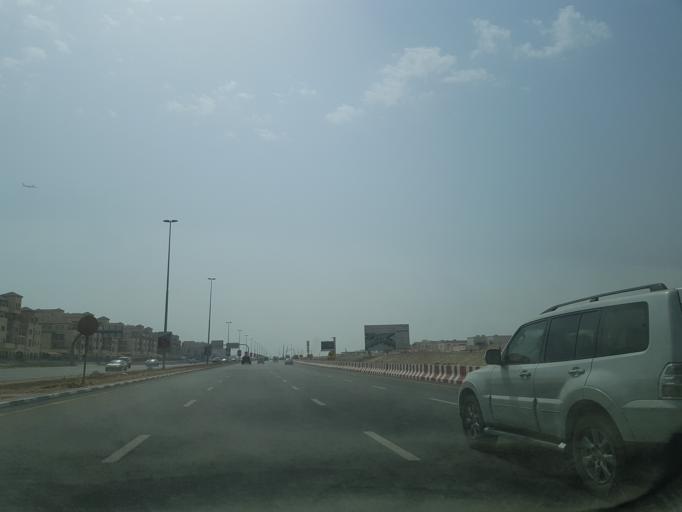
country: AE
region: Ash Shariqah
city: Sharjah
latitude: 25.2114
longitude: 55.4111
